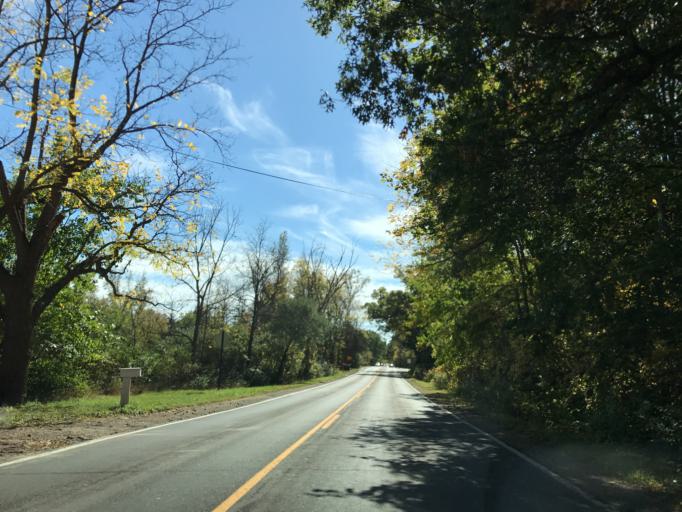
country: US
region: Michigan
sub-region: Washtenaw County
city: Ann Arbor
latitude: 42.2861
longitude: -83.6715
